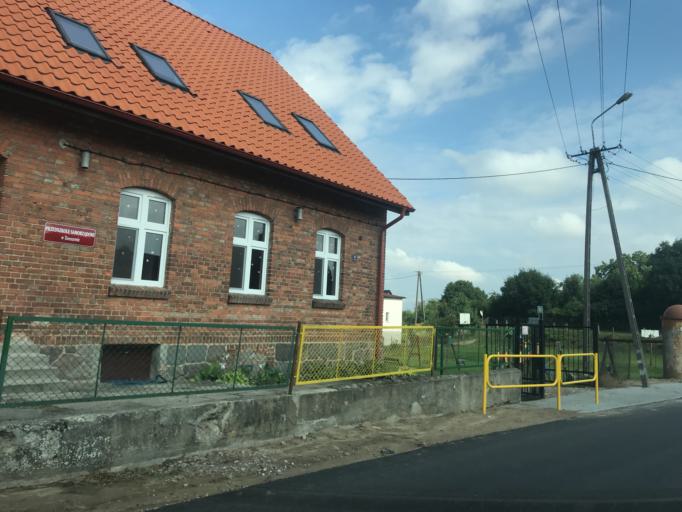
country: PL
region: Warmian-Masurian Voivodeship
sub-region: Powiat nowomiejski
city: Kurzetnik
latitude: 53.3843
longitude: 19.4669
